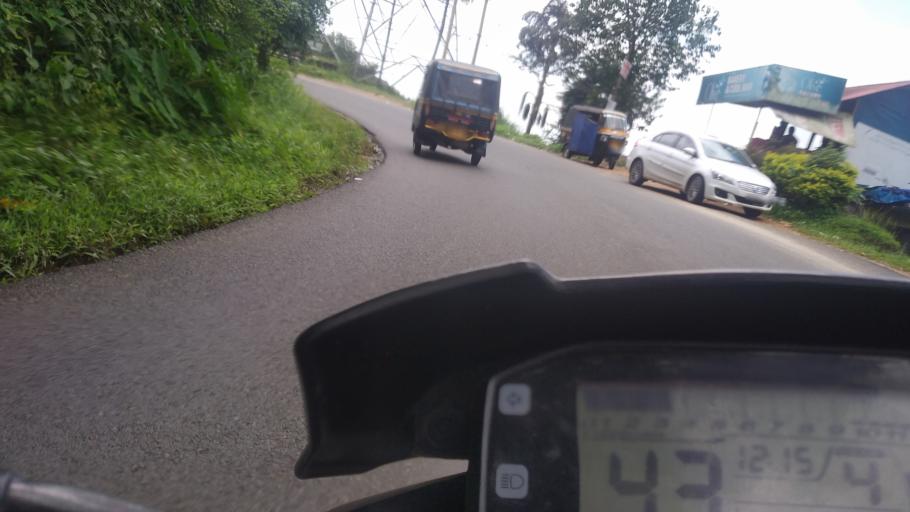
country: IN
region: Kerala
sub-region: Idukki
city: Munnar
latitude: 10.0120
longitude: 77.0083
